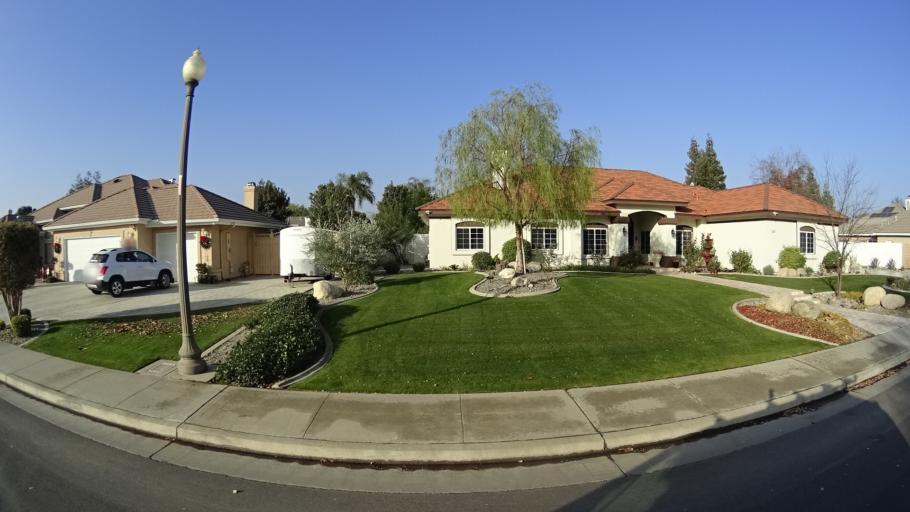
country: US
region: California
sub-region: Kern County
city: Rosedale
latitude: 35.3705
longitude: -119.1389
